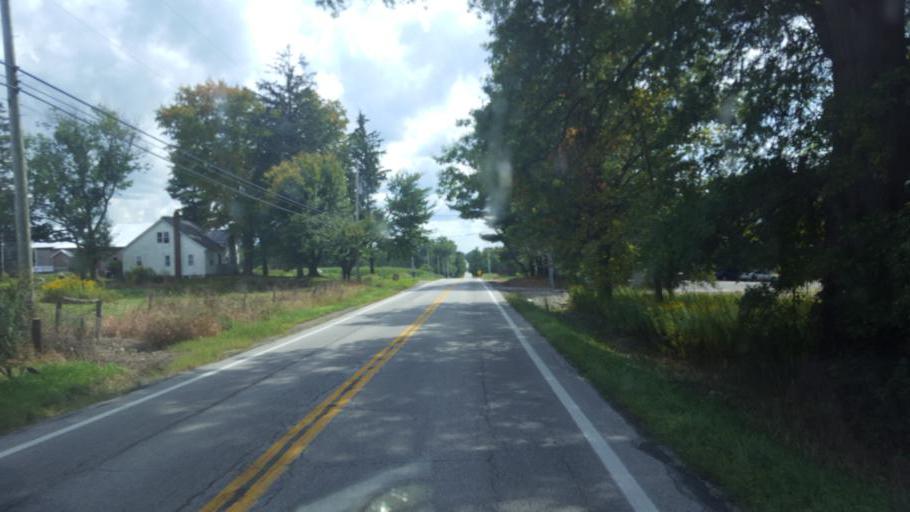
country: US
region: Ohio
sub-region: Portage County
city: Hiram
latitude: 41.3774
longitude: -81.1431
